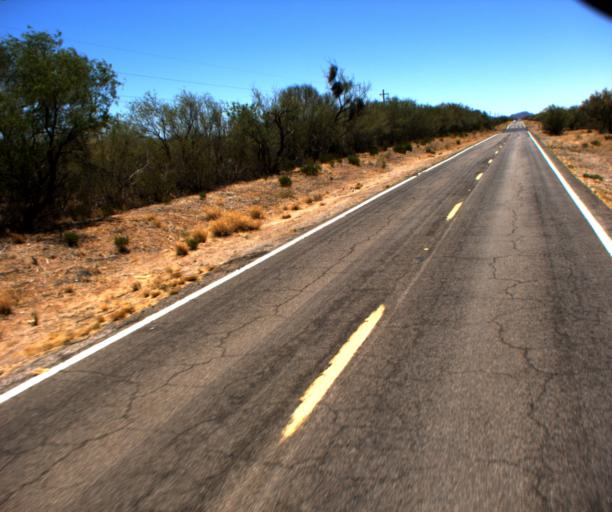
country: US
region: Arizona
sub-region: Pima County
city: Sells
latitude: 32.0554
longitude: -112.0297
